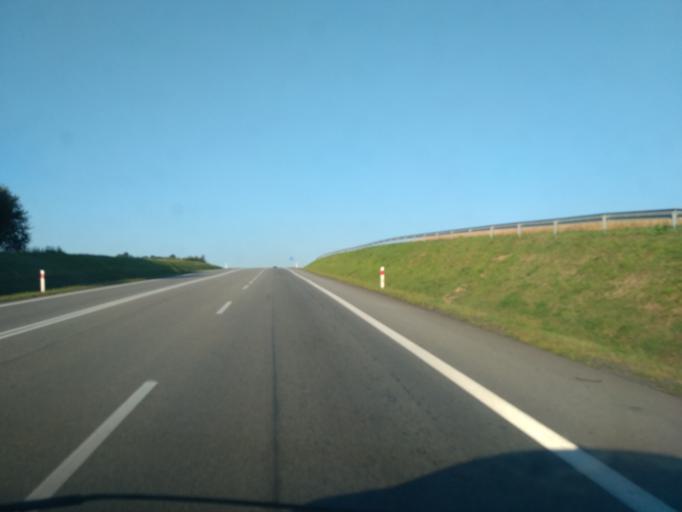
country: PL
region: Subcarpathian Voivodeship
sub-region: Powiat krosnienski
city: Miejsce Piastowe
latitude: 49.6115
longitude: 21.7449
